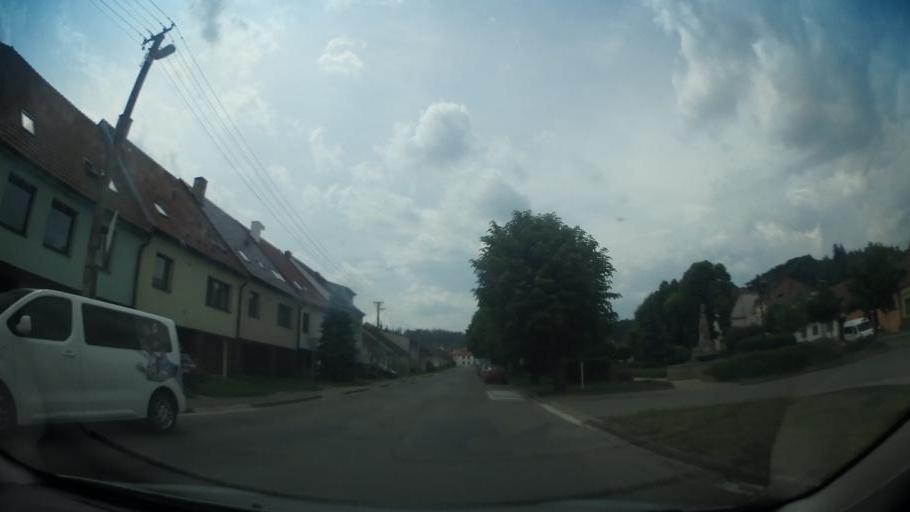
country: CZ
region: South Moravian
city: Lysice
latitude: 49.4517
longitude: 16.5375
